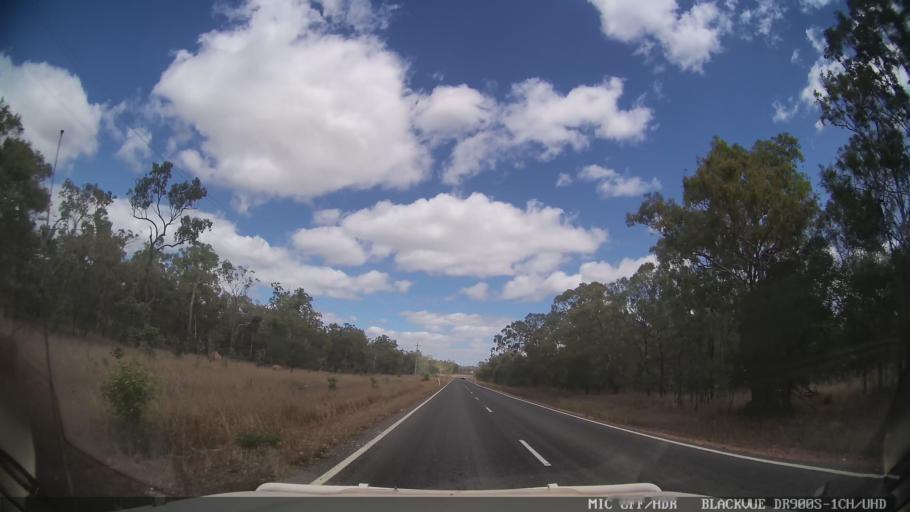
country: AU
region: Queensland
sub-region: Tablelands
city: Ravenshoe
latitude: -18.0302
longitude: 144.8699
